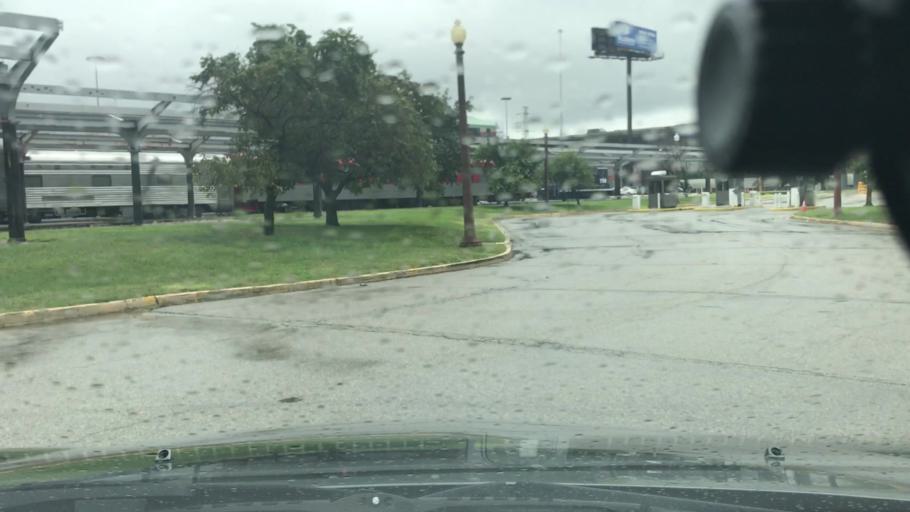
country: US
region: Missouri
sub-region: City of Saint Louis
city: St. Louis
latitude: 38.6272
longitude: -90.2101
